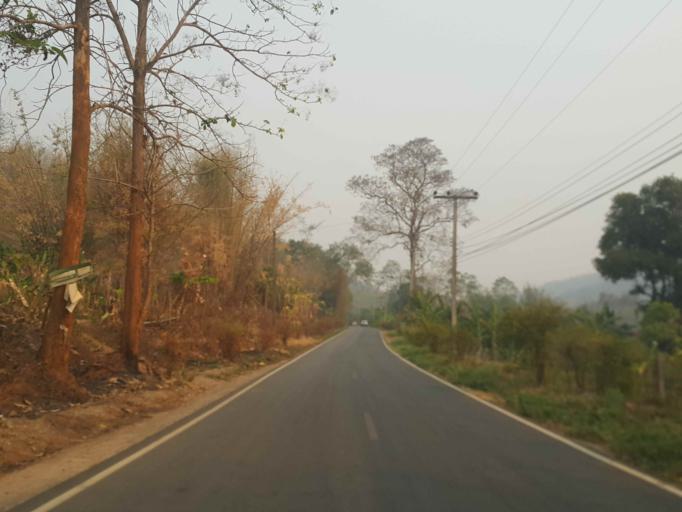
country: TH
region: Chiang Mai
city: Mae Taeng
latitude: 19.1337
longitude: 98.8800
